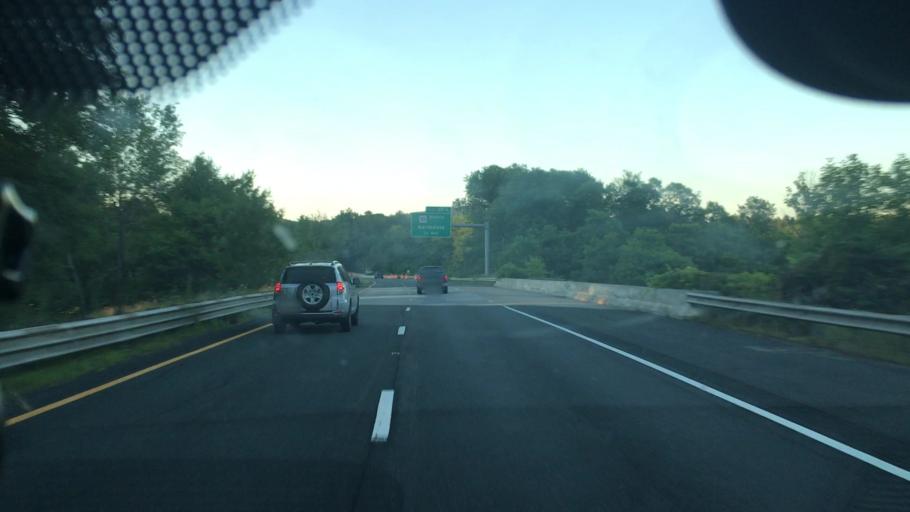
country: US
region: Massachusetts
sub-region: Franklin County
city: Bernardston
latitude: 42.6607
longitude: -72.5464
